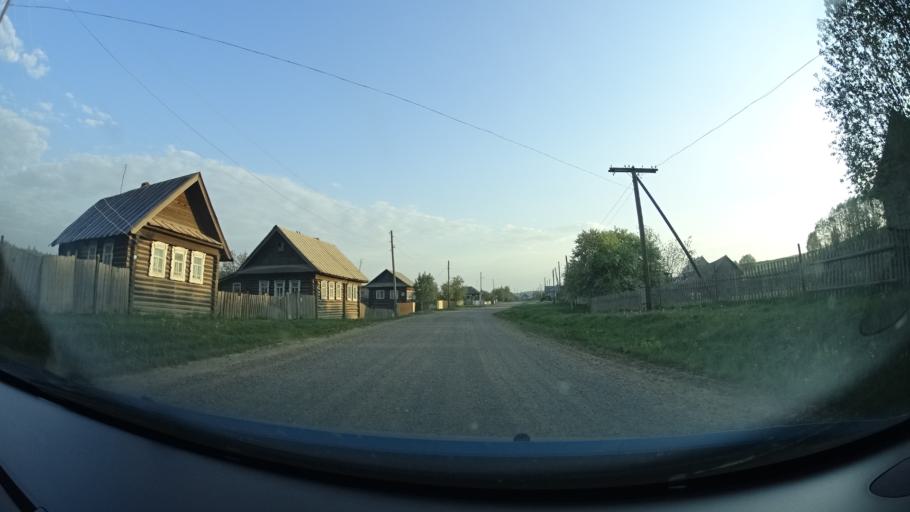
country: RU
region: Perm
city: Kuyeda
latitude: 56.6670
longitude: 55.6937
